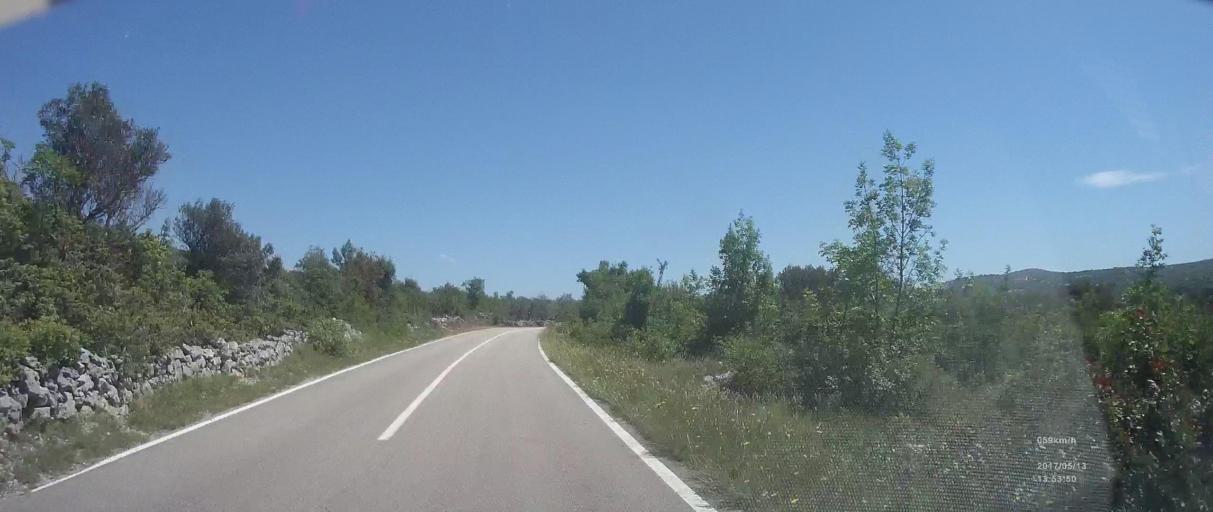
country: HR
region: Sibensko-Kniniska
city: Rogoznica
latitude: 43.5978
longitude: 16.0020
